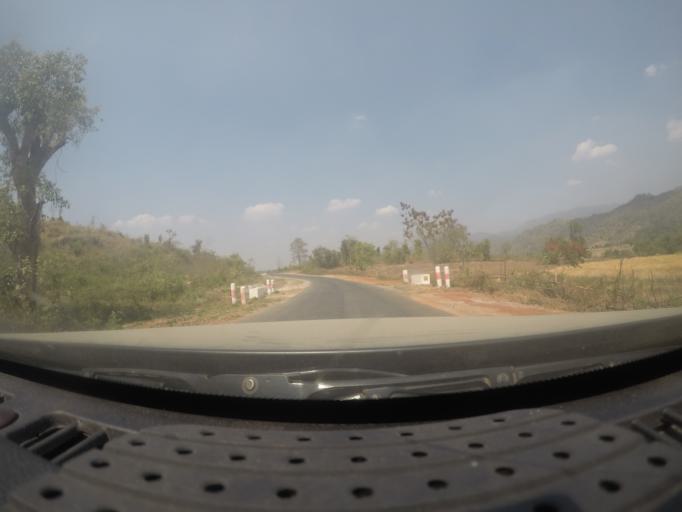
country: MM
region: Shan
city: Taunggyi
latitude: 21.0710
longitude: 96.5150
